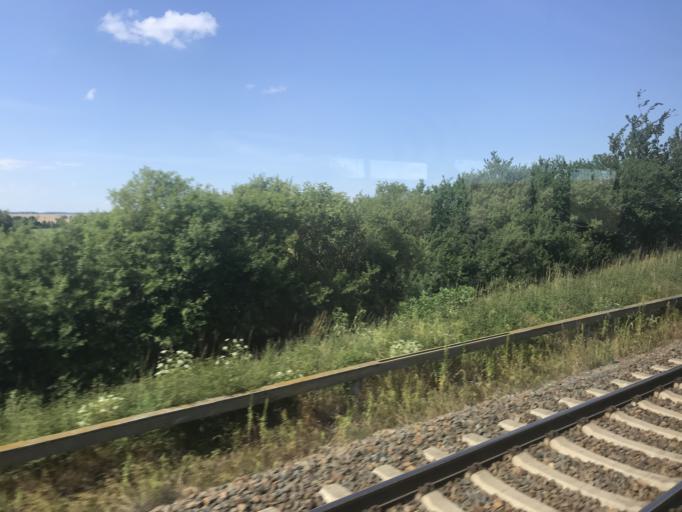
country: DE
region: Brandenburg
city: Angermunde
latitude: 53.0882
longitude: 14.0021
